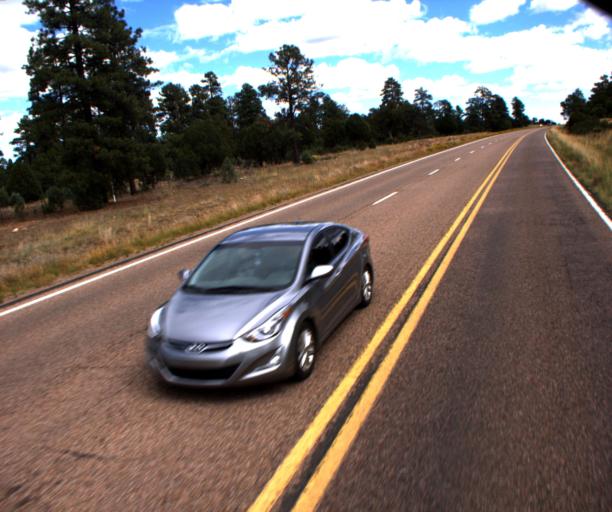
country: US
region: Arizona
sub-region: Navajo County
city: Heber-Overgaard
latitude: 34.4338
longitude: -110.6378
